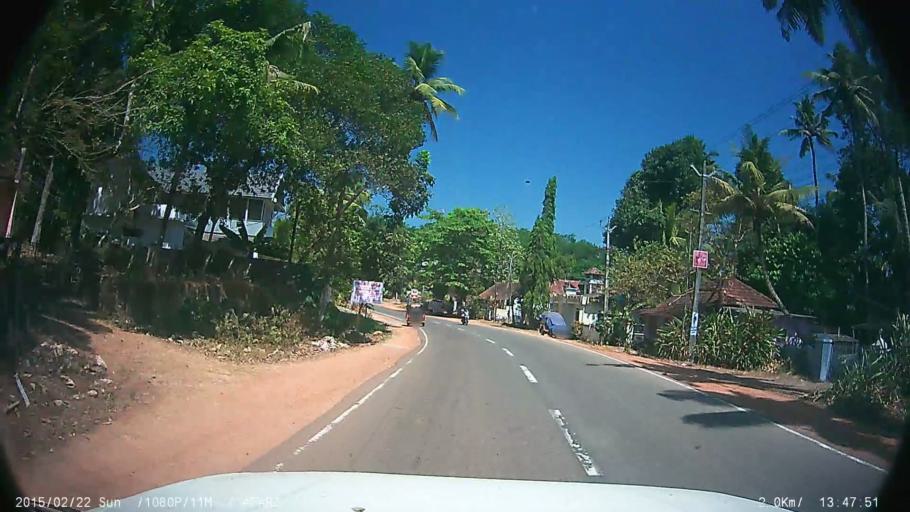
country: IN
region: Kerala
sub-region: Kottayam
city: Changanacheri
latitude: 9.4921
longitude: 76.6232
